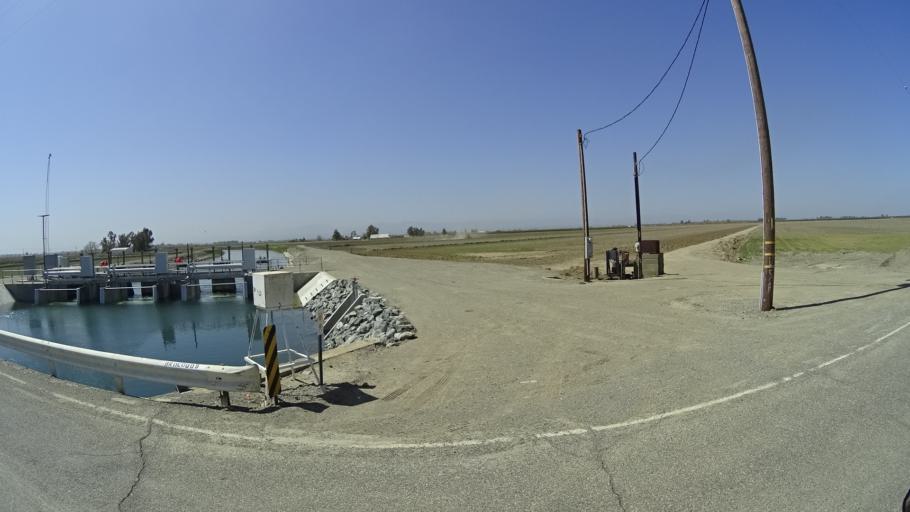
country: US
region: California
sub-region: Glenn County
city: Willows
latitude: 39.5568
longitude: -122.1369
